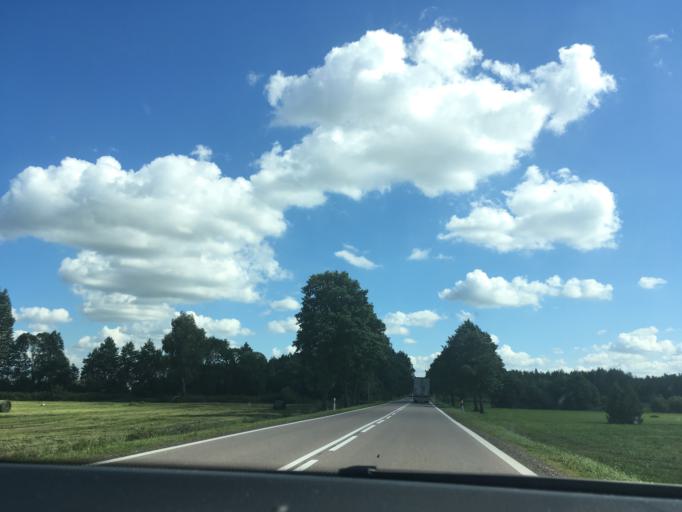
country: PL
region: Podlasie
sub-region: Powiat sokolski
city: Suchowola
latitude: 53.6687
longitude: 23.1212
